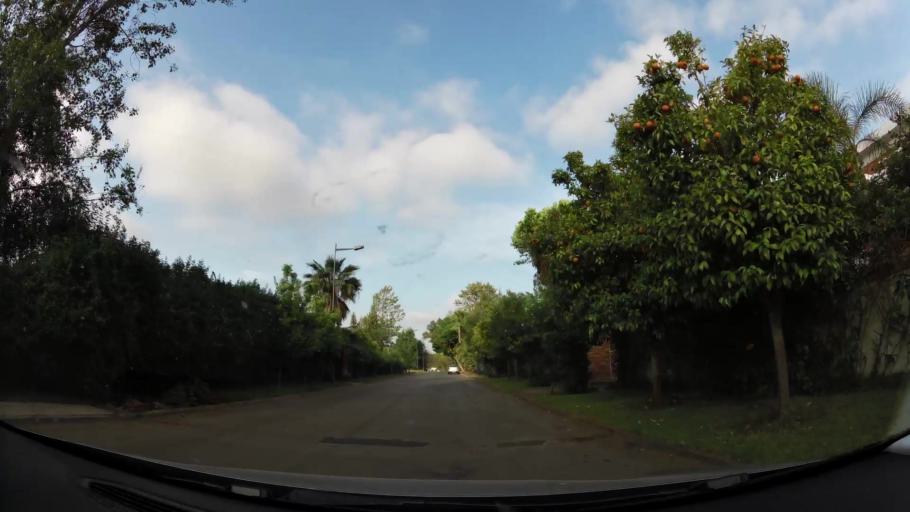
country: MA
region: Rabat-Sale-Zemmour-Zaer
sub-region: Rabat
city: Rabat
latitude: 33.9450
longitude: -6.8151
